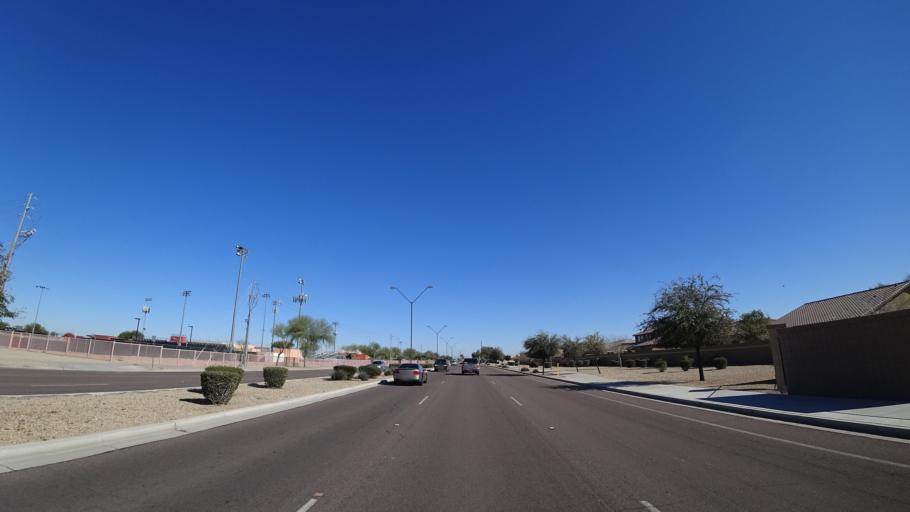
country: US
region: Arizona
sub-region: Maricopa County
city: Goodyear
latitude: 33.4355
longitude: -112.4033
